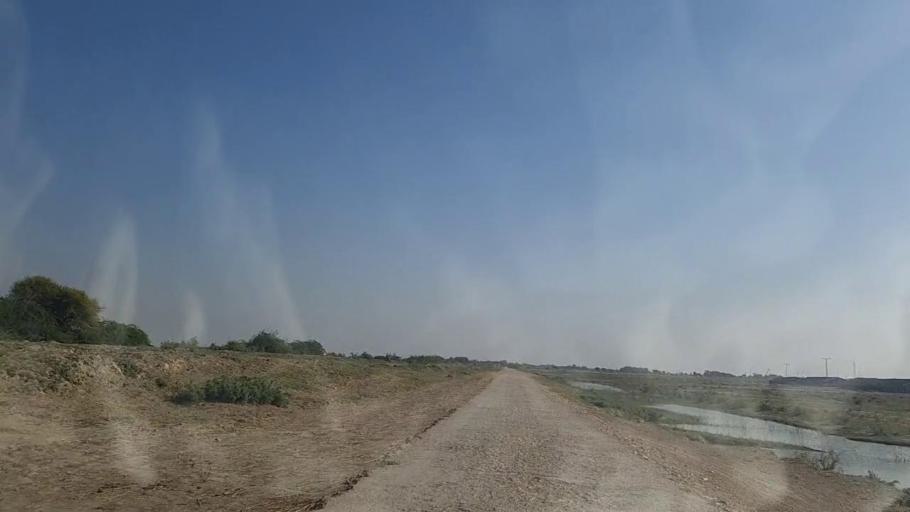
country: PK
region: Sindh
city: Mirpur Batoro
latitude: 24.6104
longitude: 68.1691
